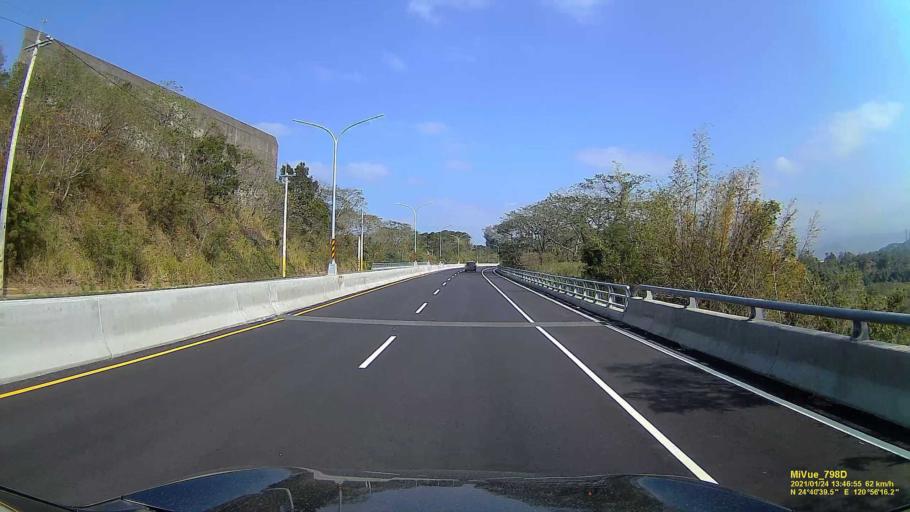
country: TW
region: Taiwan
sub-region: Hsinchu
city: Hsinchu
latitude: 24.6778
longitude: 120.9406
